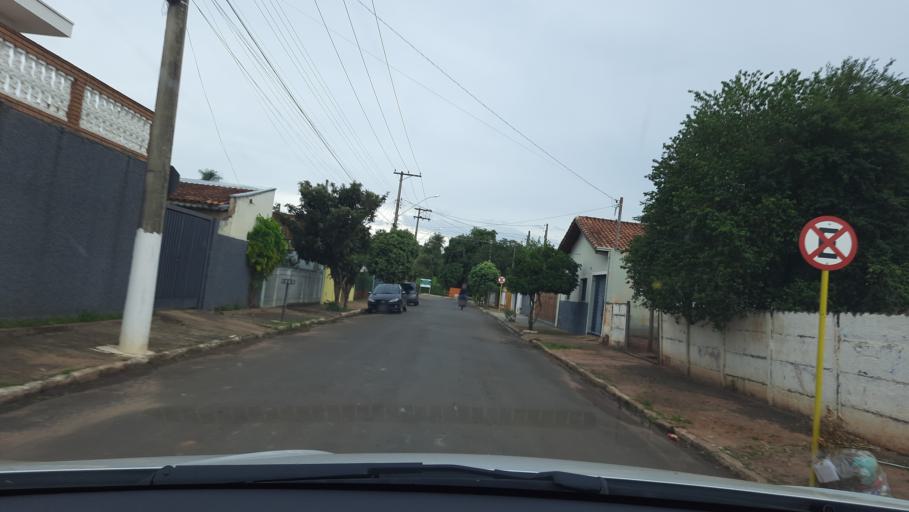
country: BR
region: Sao Paulo
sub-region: Casa Branca
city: Casa Branca
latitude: -21.7682
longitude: -47.0895
